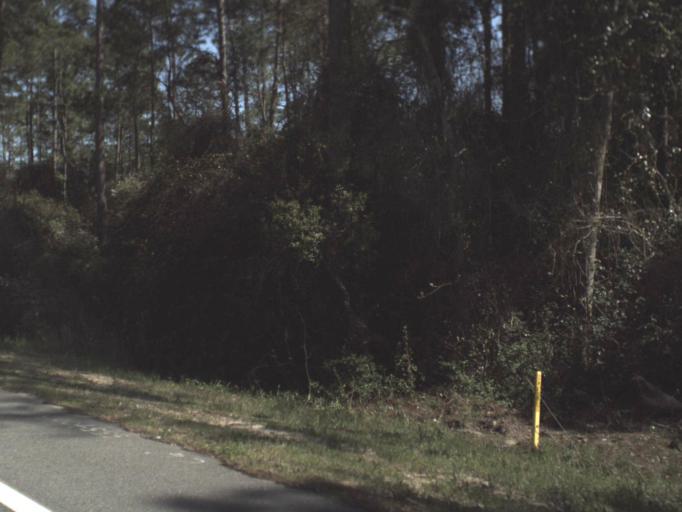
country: US
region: Florida
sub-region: Bay County
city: Lynn Haven
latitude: 30.3230
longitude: -85.6924
